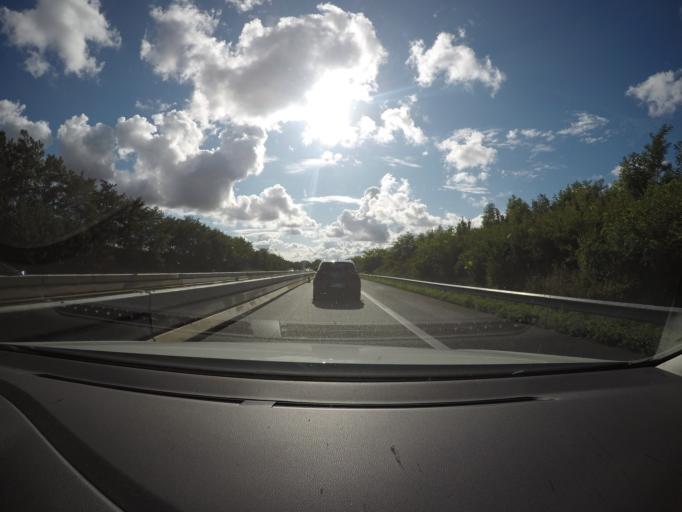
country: FR
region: Nord-Pas-de-Calais
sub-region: Departement du Nord
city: Fontaine-Notre-Dame
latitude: 50.1497
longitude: 3.1375
